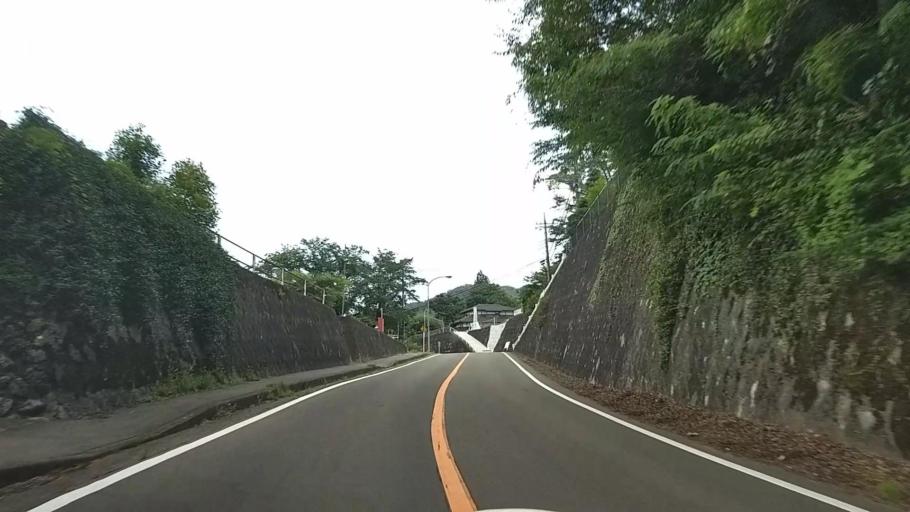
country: JP
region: Yamanashi
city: Uenohara
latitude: 35.6120
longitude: 139.1481
